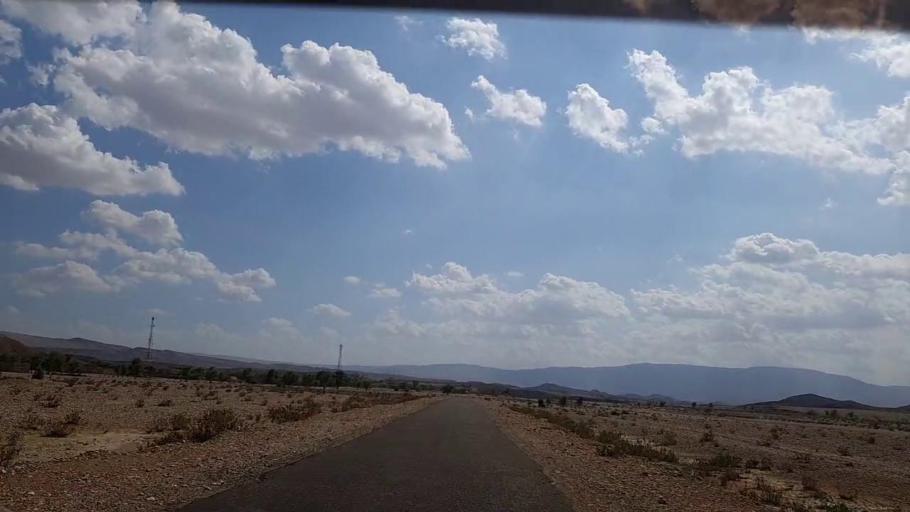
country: PK
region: Sindh
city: Johi
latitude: 26.5019
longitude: 67.4375
